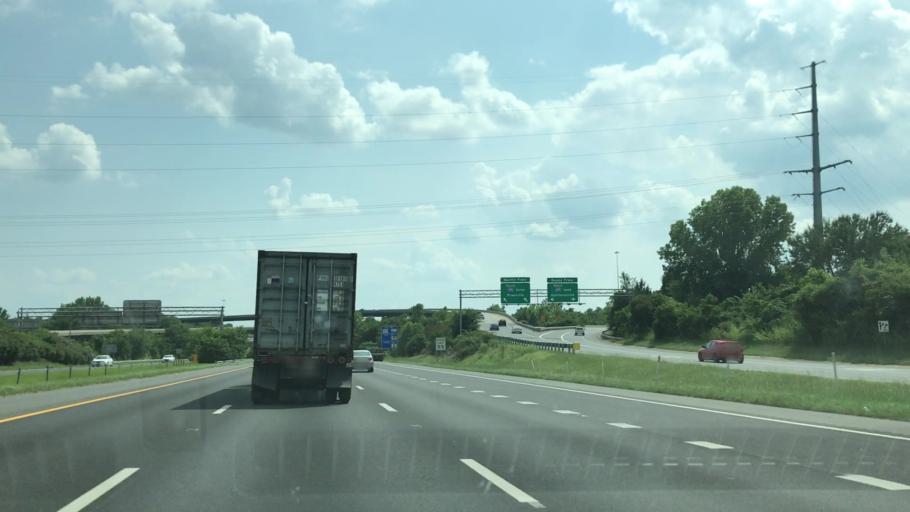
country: US
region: North Carolina
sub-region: Mecklenburg County
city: Pineville
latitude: 35.1298
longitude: -80.9150
